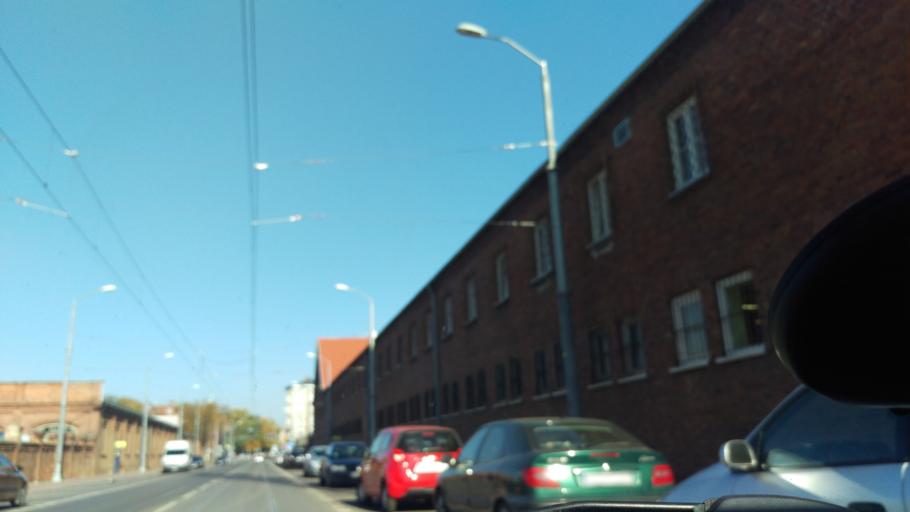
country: PL
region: West Pomeranian Voivodeship
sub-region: Szczecin
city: Szczecin
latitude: 53.4190
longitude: 14.5447
